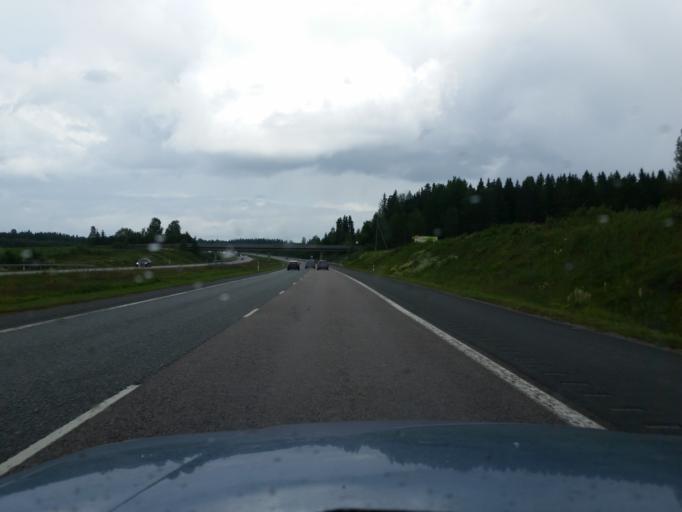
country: FI
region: Paijanne Tavastia
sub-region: Lahti
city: Nastola
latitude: 61.0740
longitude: 25.8859
